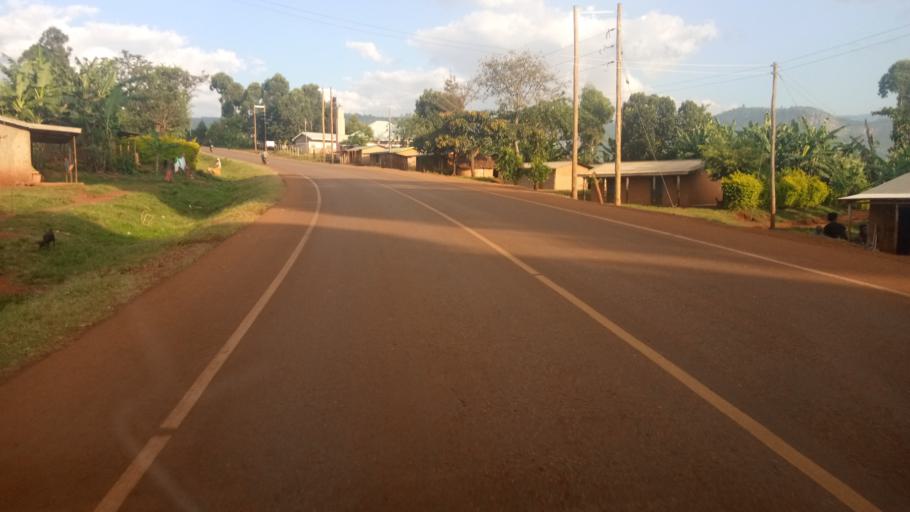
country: UG
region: Eastern Region
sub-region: Sironko District
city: Sironko
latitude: 1.3193
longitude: 34.3392
